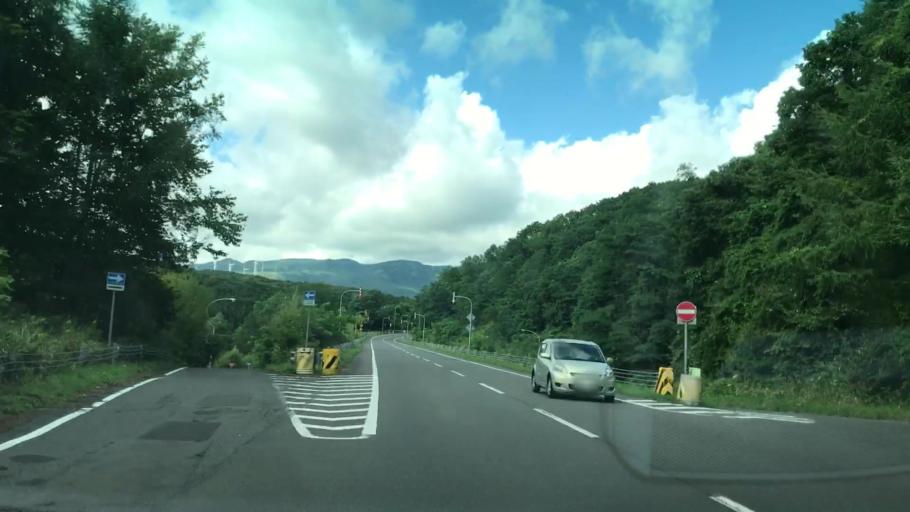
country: JP
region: Hokkaido
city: Muroran
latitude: 42.3728
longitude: 140.9613
